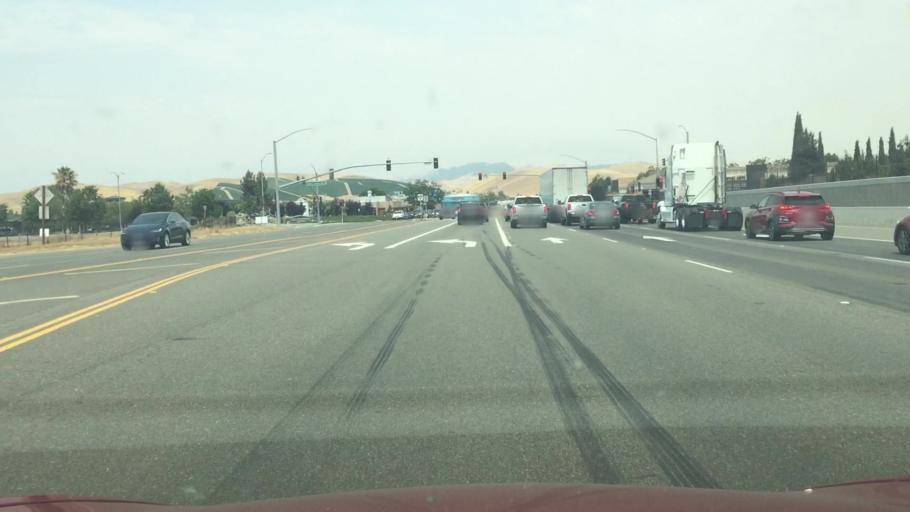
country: US
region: California
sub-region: Alameda County
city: Livermore
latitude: 37.6878
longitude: -121.8057
